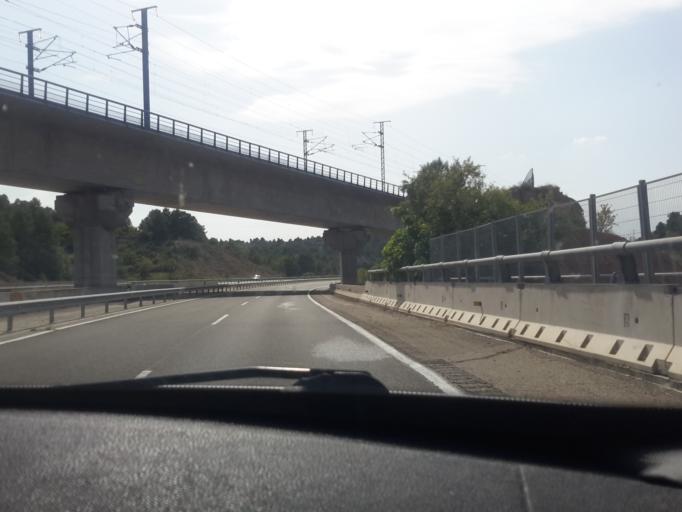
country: ES
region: Catalonia
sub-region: Provincia de Lleida
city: Vinaixa
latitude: 41.4186
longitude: 0.9727
